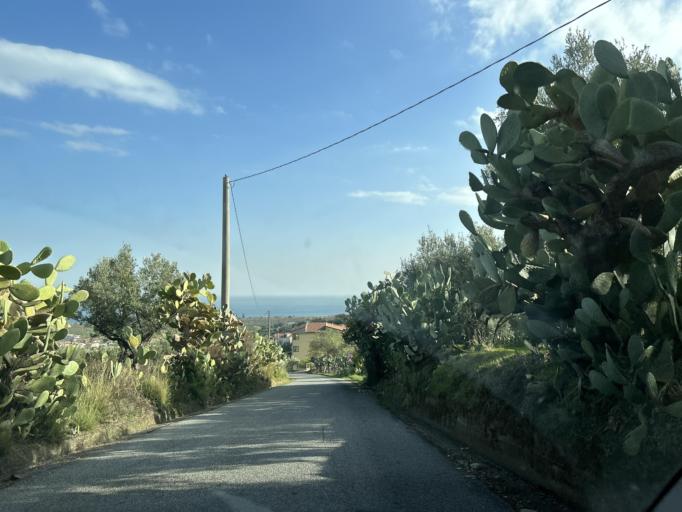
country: IT
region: Calabria
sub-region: Provincia di Catanzaro
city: Montepaone
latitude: 38.7167
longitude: 16.5167
